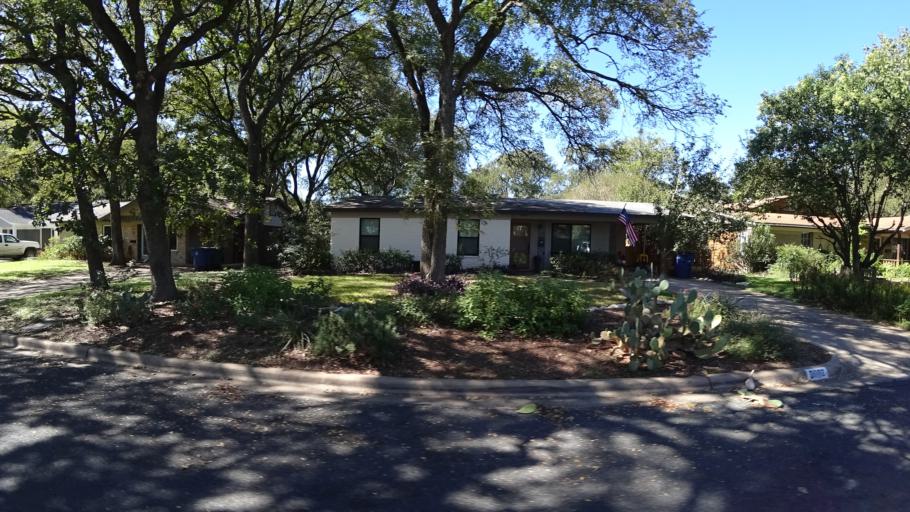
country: US
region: Texas
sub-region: Travis County
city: Rollingwood
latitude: 30.2194
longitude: -97.7879
